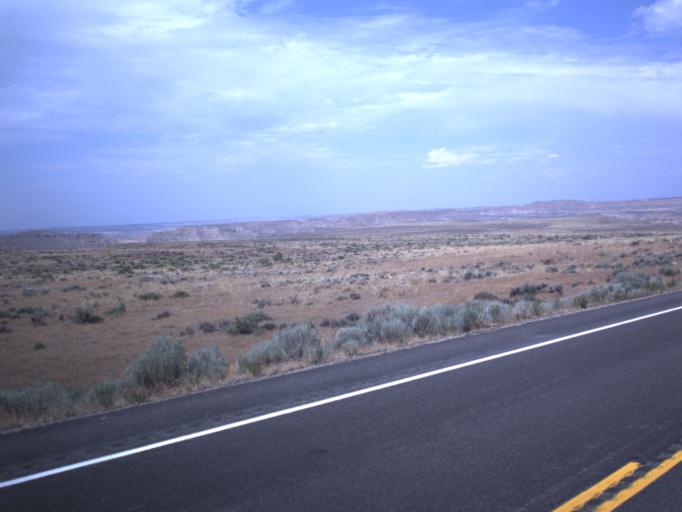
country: US
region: Utah
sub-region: Uintah County
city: Naples
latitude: 40.2850
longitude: -109.4717
